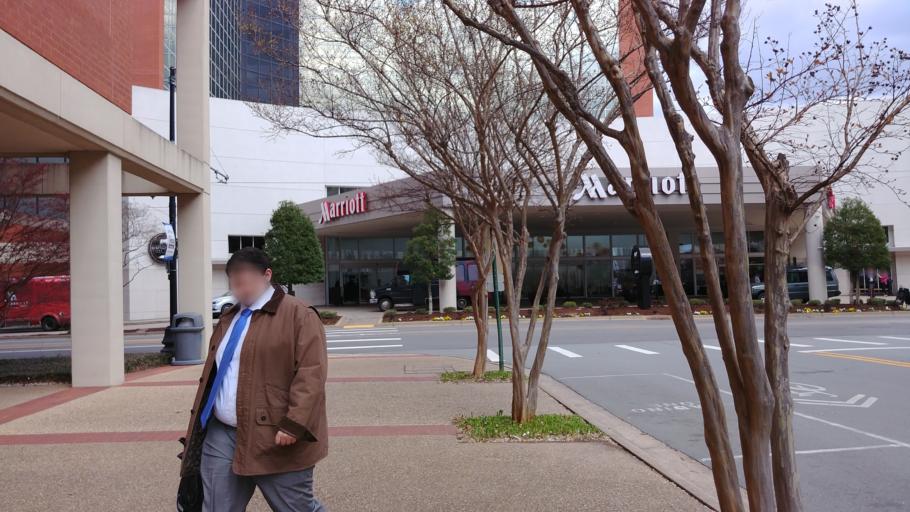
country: US
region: Arkansas
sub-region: Pulaski County
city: Little Rock
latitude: 34.7480
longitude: -92.2717
